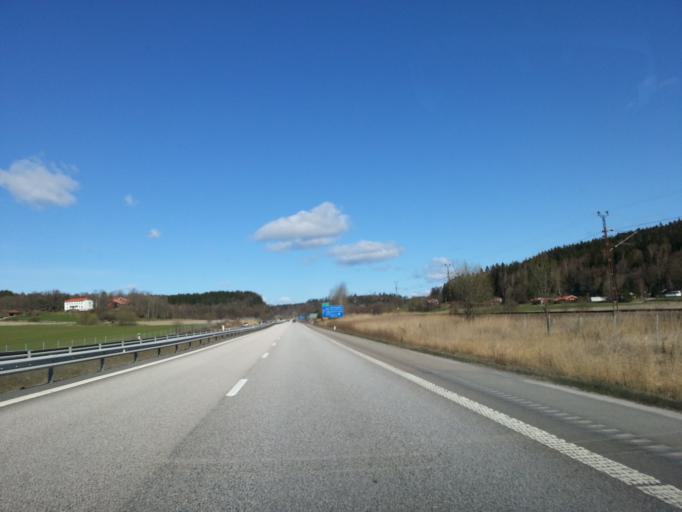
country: SE
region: Vaestra Goetaland
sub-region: Uddevalla Kommun
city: Ljungskile
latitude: 58.2795
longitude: 11.8830
